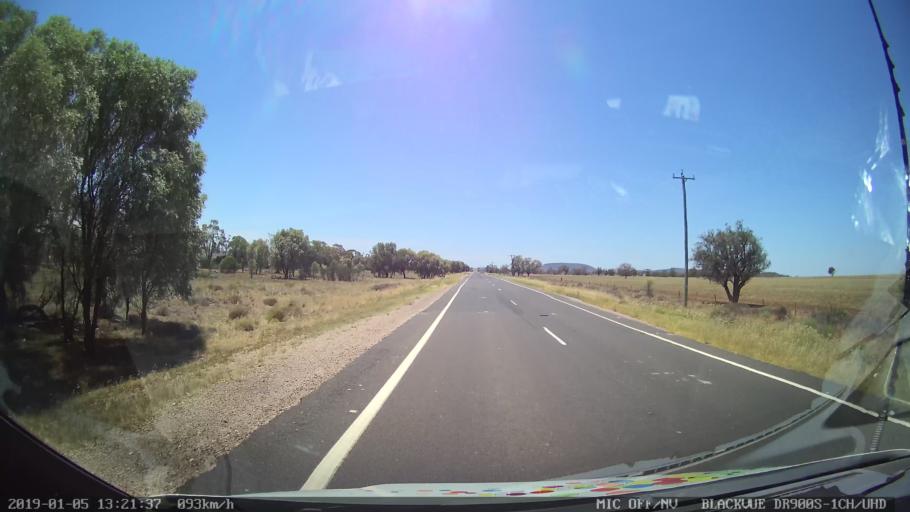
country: AU
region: New South Wales
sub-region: Gunnedah
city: Gunnedah
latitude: -31.0930
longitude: 149.9509
